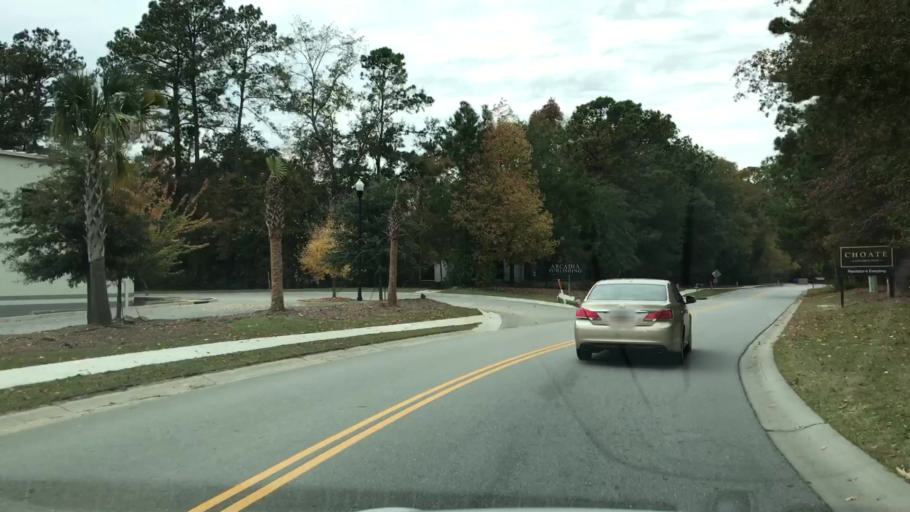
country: US
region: South Carolina
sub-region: Charleston County
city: Mount Pleasant
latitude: 32.8448
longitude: -79.8755
